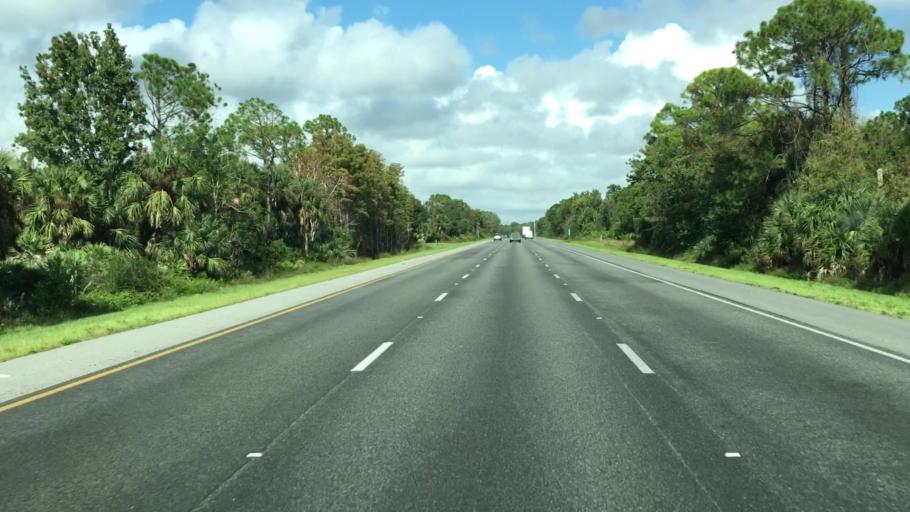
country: US
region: Florida
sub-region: Volusia County
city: Glencoe
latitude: 29.0541
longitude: -81.0073
